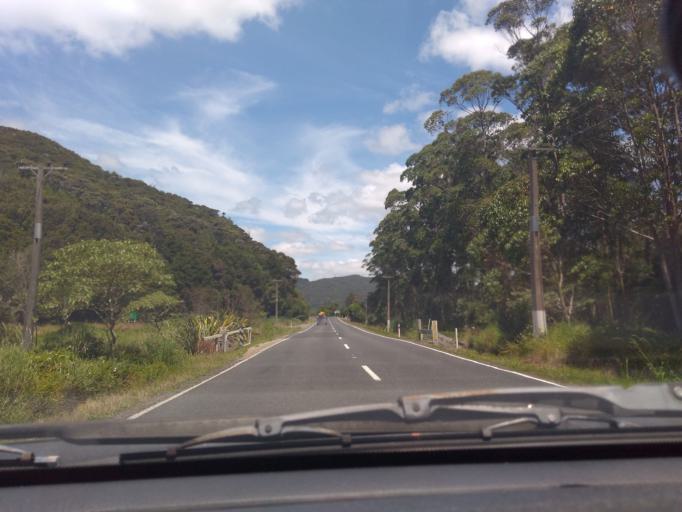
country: NZ
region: Northland
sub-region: Far North District
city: Kerikeri
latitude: -35.0863
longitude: 173.7651
